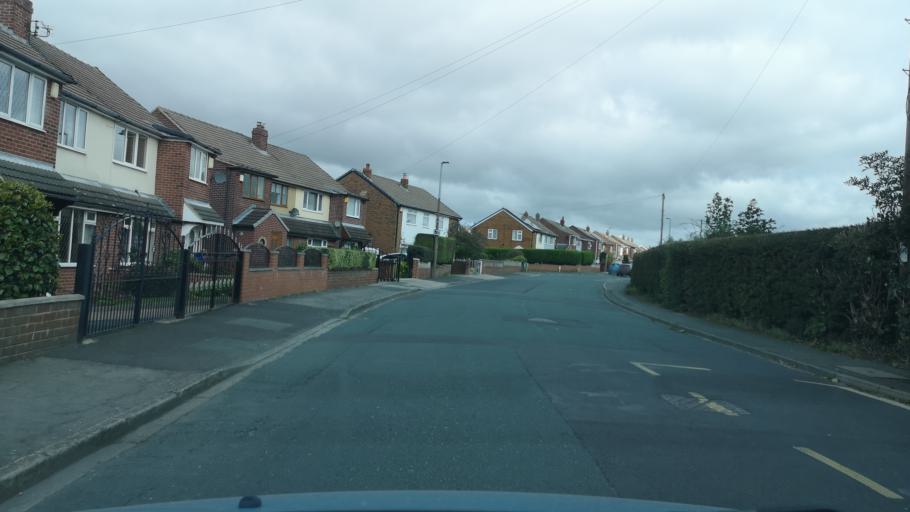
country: GB
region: England
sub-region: City and Borough of Leeds
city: Drighlington
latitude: 53.7311
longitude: -1.6490
